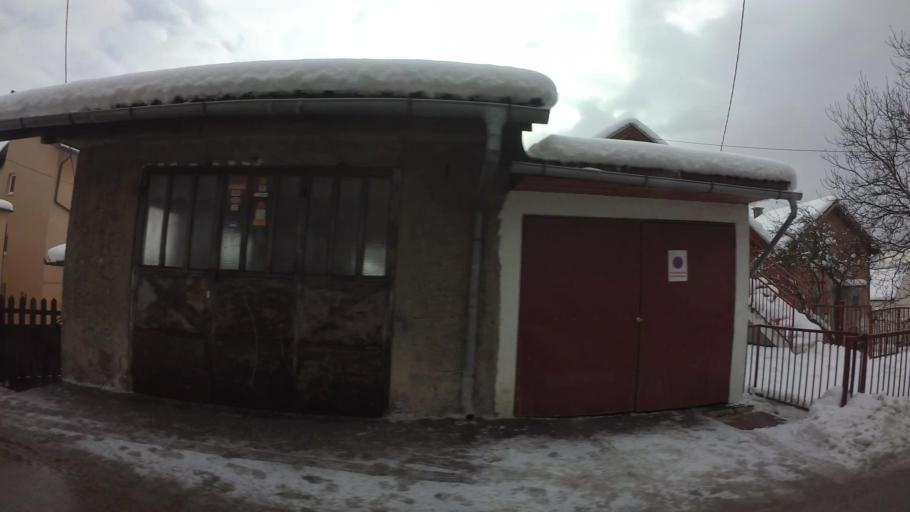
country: BA
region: Federation of Bosnia and Herzegovina
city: Kobilja Glava
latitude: 43.8732
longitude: 18.4372
